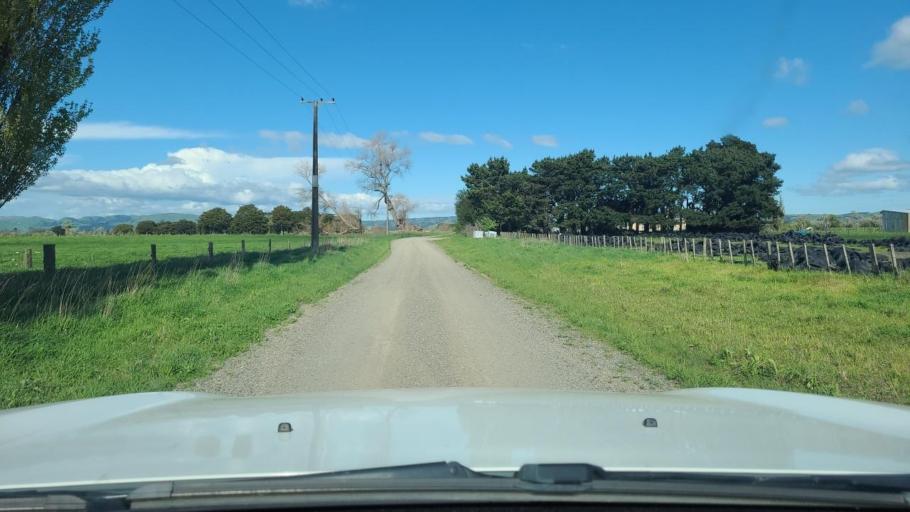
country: NZ
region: Wellington
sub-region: South Wairarapa District
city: Waipawa
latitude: -41.2108
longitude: 175.3933
